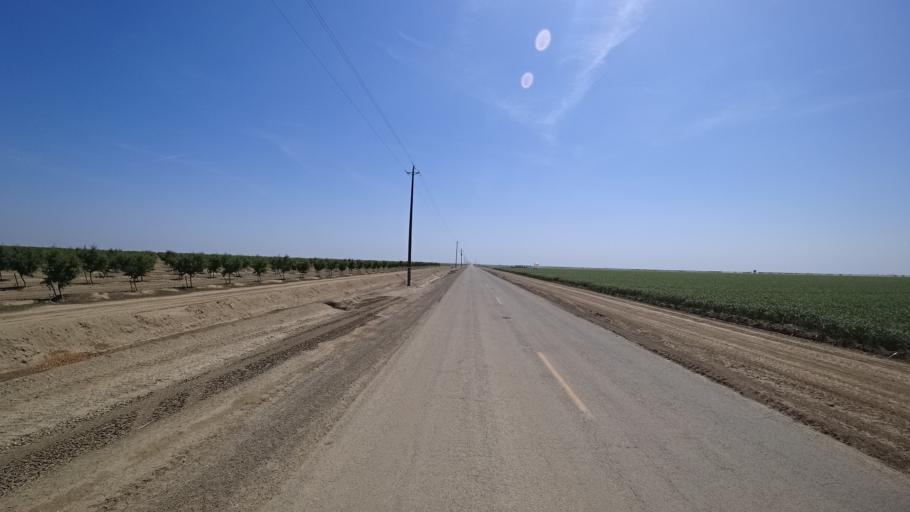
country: US
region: California
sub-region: Kings County
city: Kettleman City
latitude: 36.0943
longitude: -119.9794
